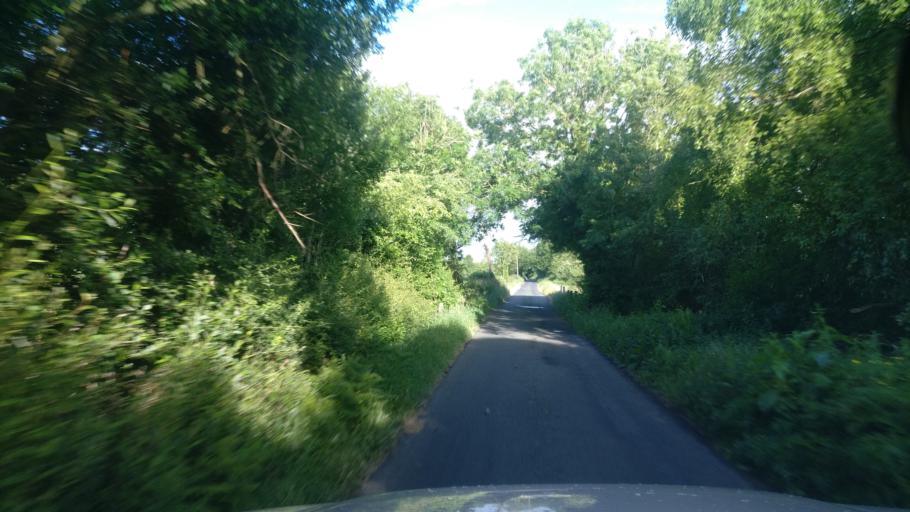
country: IE
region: Connaught
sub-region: County Galway
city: Ballinasloe
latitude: 53.2402
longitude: -8.1877
